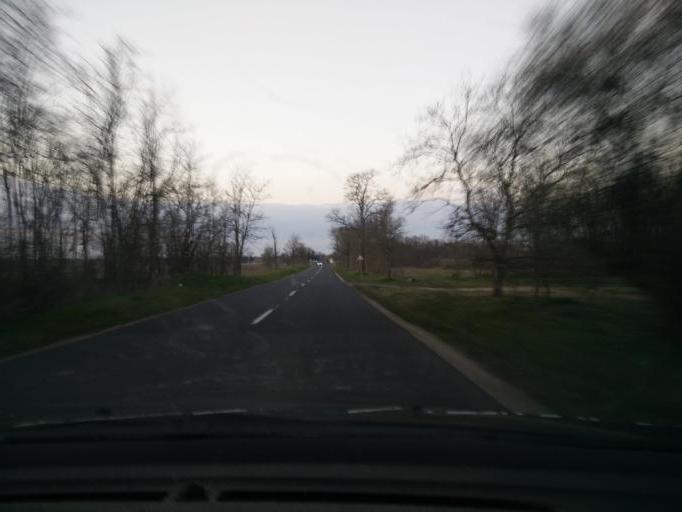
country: HU
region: Veszprem
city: Csabrendek
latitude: 47.0550
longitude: 17.3385
